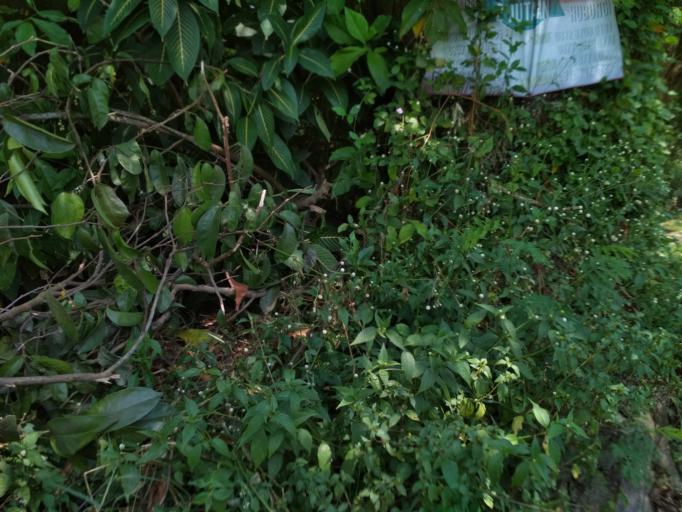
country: ID
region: West Java
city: Ciampea
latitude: -6.5516
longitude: 106.7360
